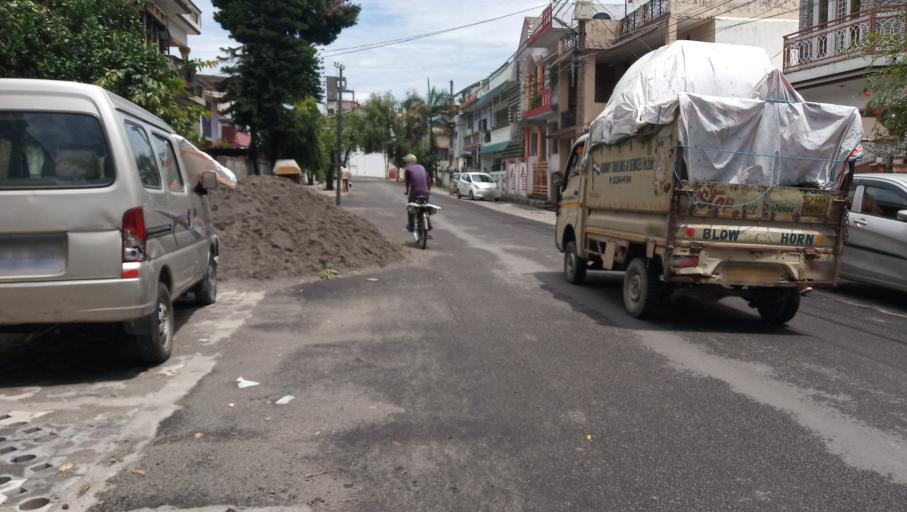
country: IN
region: Uttarakhand
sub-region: Dehradun
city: Dehradun
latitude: 30.3651
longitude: 78.0660
